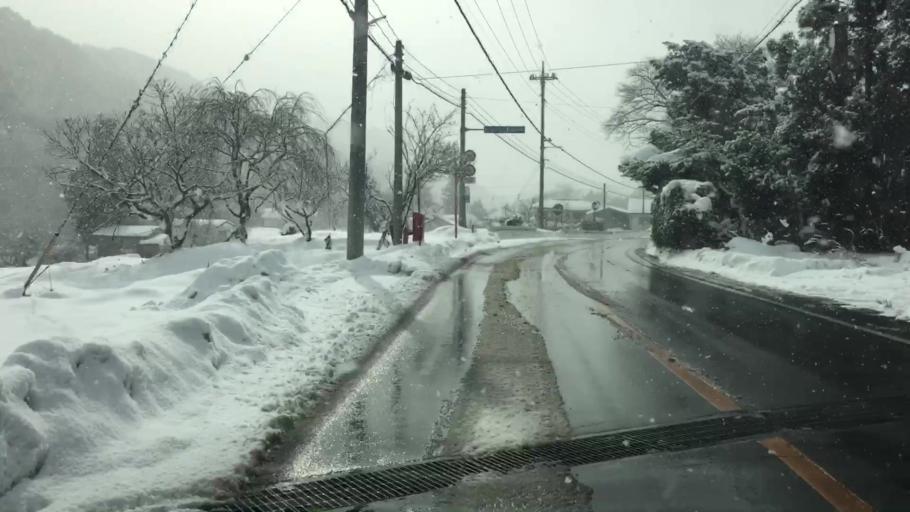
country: JP
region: Gunma
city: Numata
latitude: 36.7003
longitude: 139.0650
